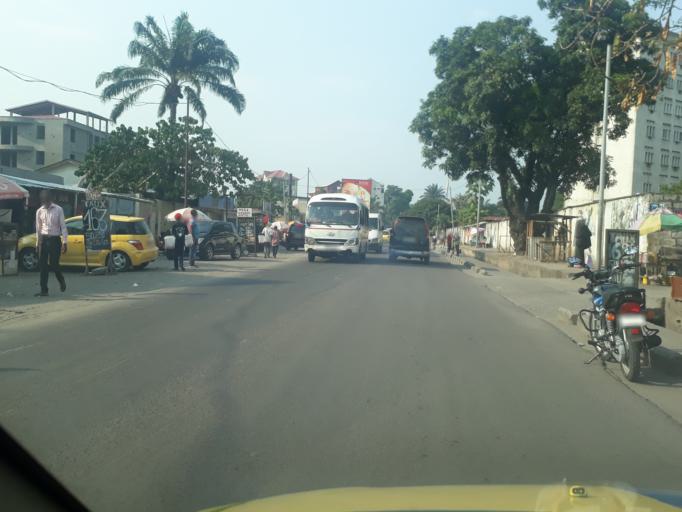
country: CD
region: Kinshasa
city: Kinshasa
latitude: -4.3174
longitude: 15.3304
